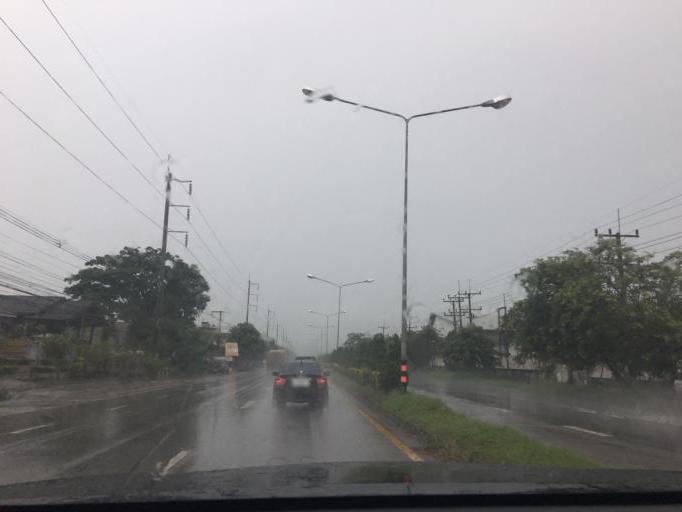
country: TH
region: Chiang Rai
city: Mae Fa Luang
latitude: 20.2377
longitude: 99.8561
